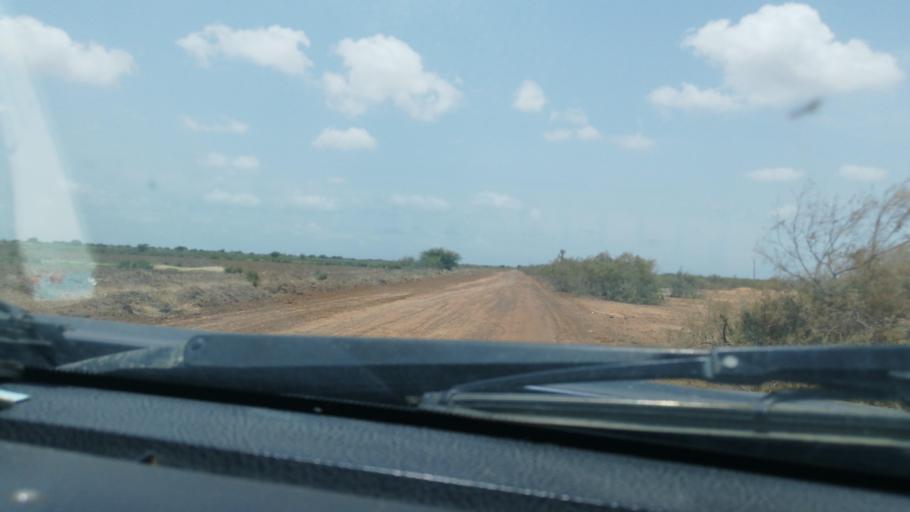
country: SN
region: Saint-Louis
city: Saint-Louis
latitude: 16.2834
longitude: -16.1935
